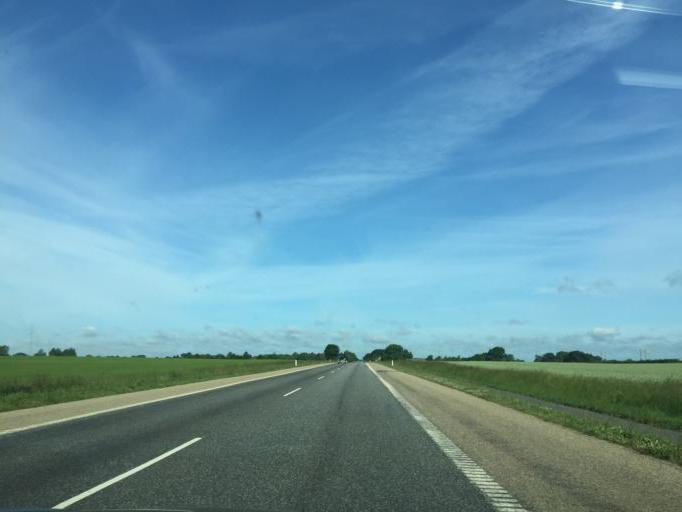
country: DK
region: South Denmark
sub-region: Middelfart Kommune
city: Strib
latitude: 55.4895
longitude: 9.8024
